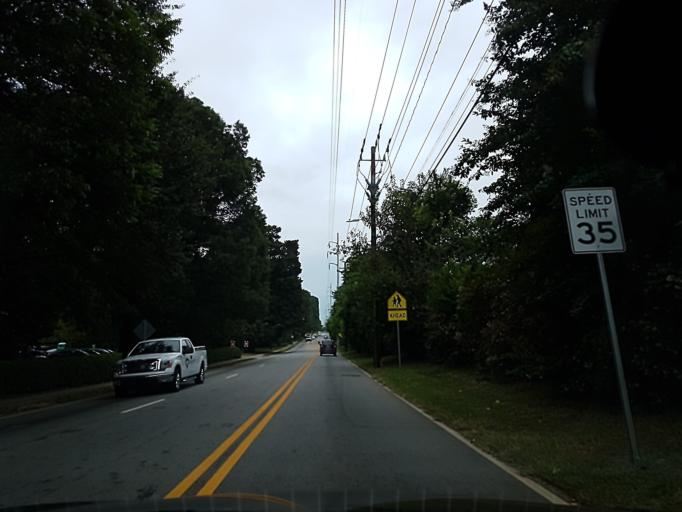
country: US
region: Georgia
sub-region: DeKalb County
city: Decatur
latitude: 33.7709
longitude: -84.2933
